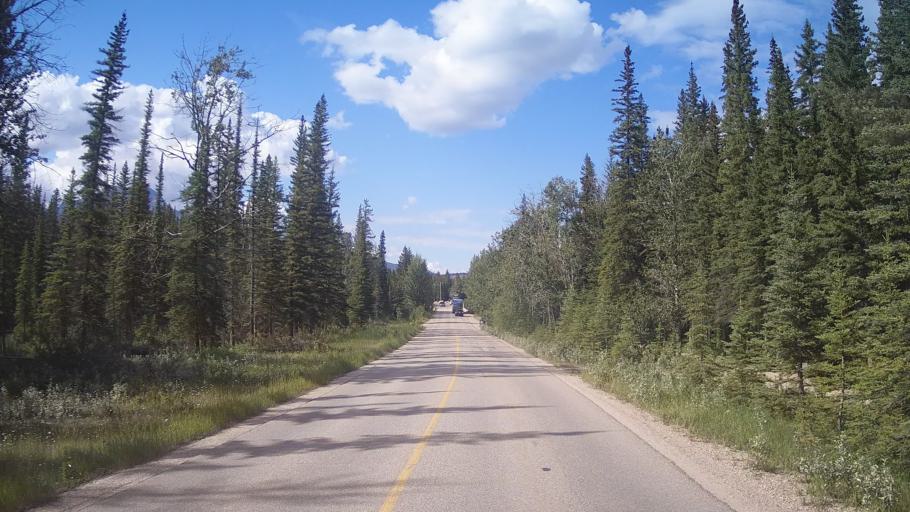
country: CA
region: Alberta
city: Jasper Park Lodge
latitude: 52.8634
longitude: -118.0702
